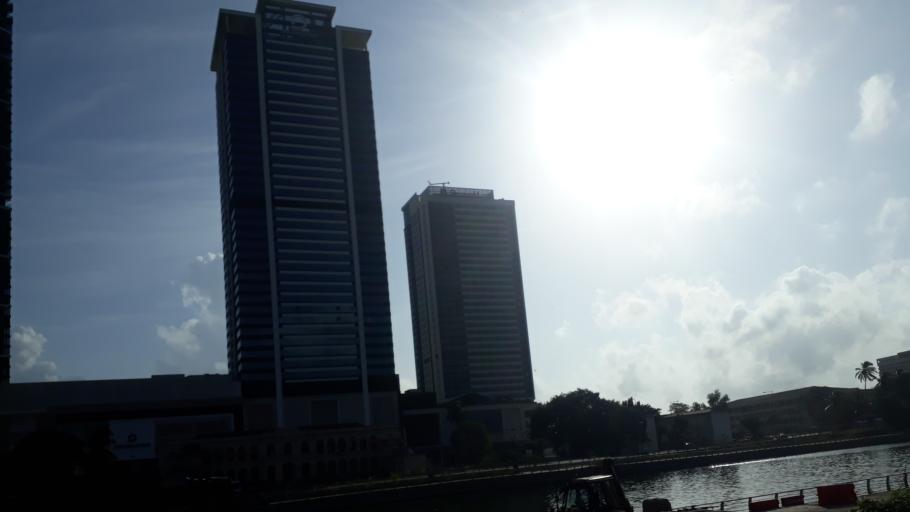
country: LK
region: Western
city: Colombo
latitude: 6.9280
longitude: 79.8475
